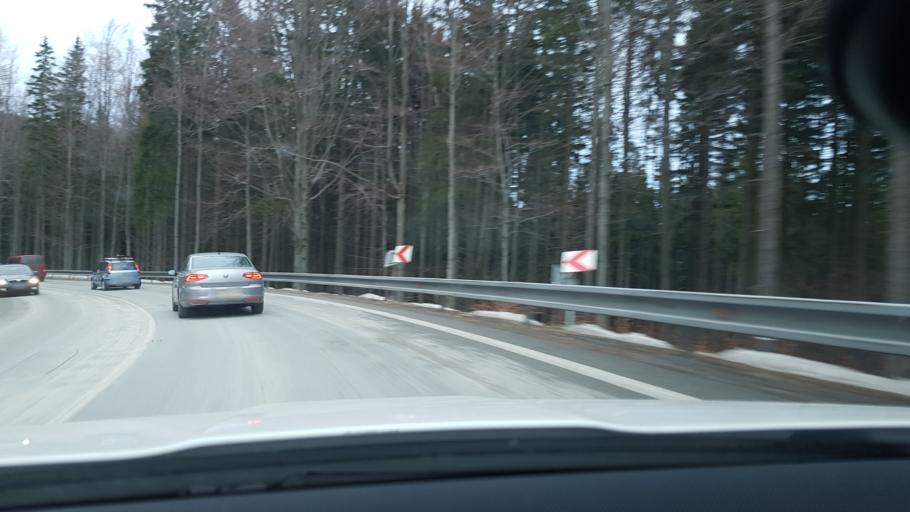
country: CZ
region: Olomoucky
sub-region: Okres Jesenik
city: Jesenik
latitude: 50.1481
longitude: 17.1697
